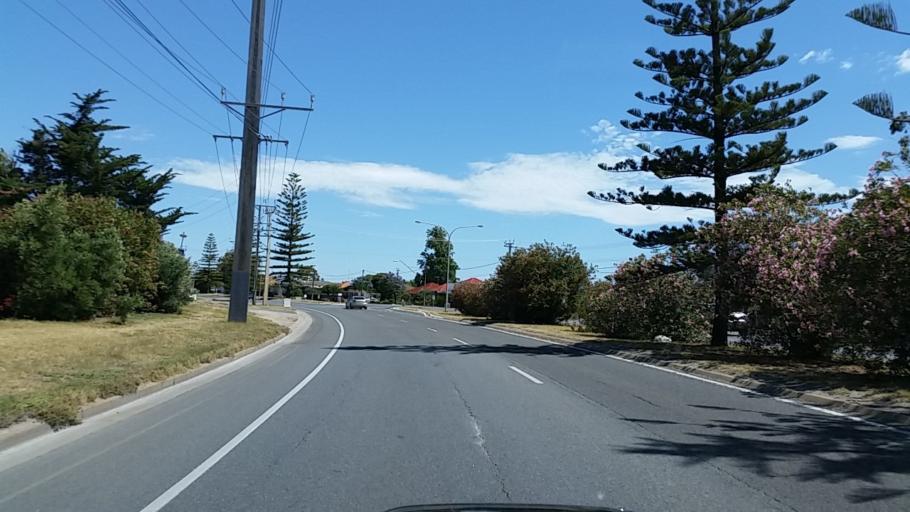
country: AU
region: South Australia
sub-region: Port Adelaide Enfield
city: Birkenhead
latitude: -34.8223
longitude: 138.4999
